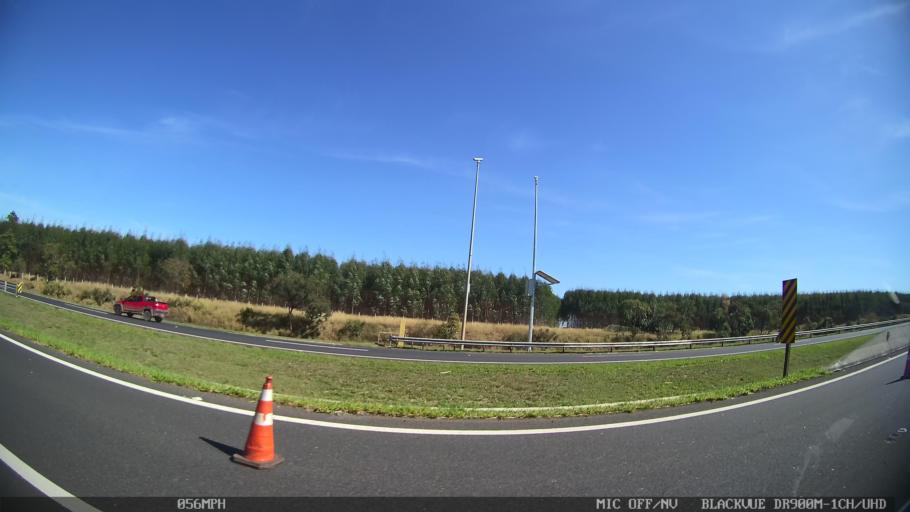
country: BR
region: Sao Paulo
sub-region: Sao Simao
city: Sao Simao
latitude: -21.5688
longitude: -47.6318
